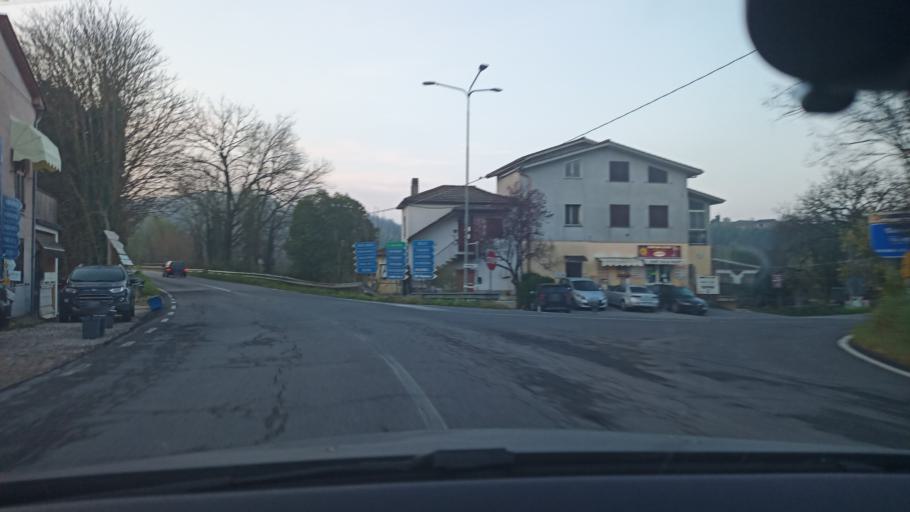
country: IT
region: Latium
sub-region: Provincia di Rieti
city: Cantalupo in Sabina
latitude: 42.2741
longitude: 12.6398
